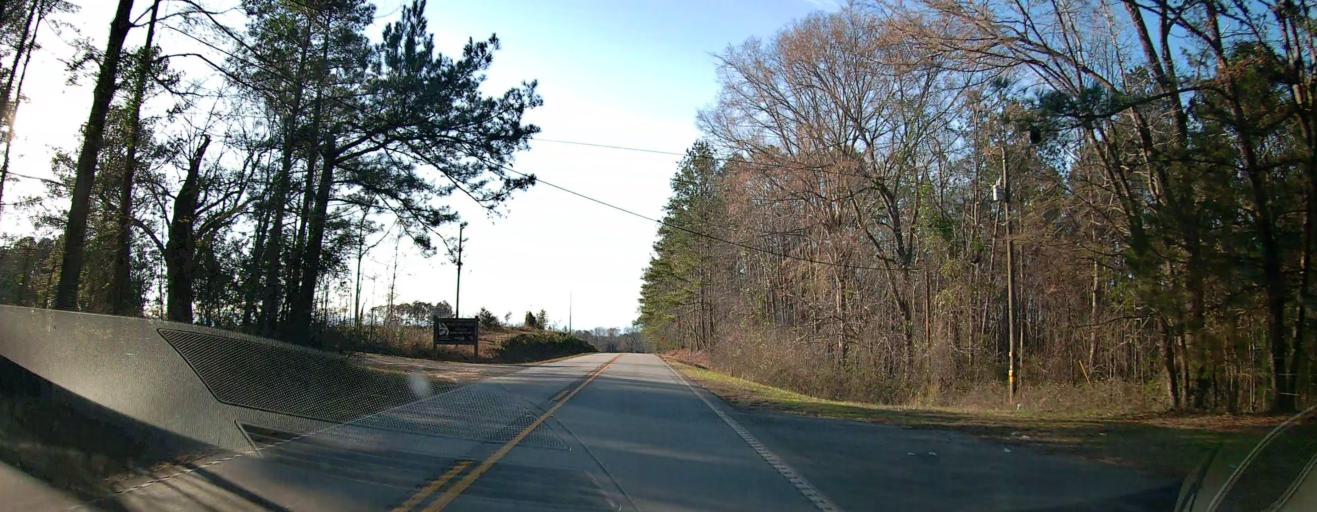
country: US
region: Alabama
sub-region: Chambers County
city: Valley
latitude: 32.7760
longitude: -85.0851
